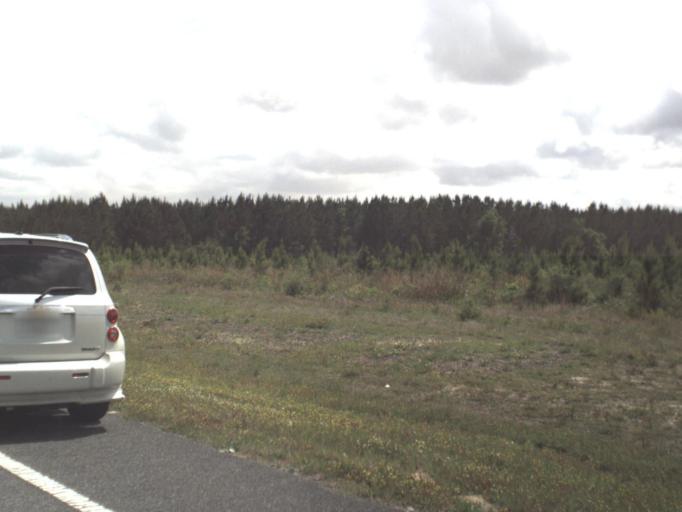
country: US
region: Florida
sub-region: Santa Rosa County
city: Wallace
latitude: 30.8230
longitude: -87.1357
